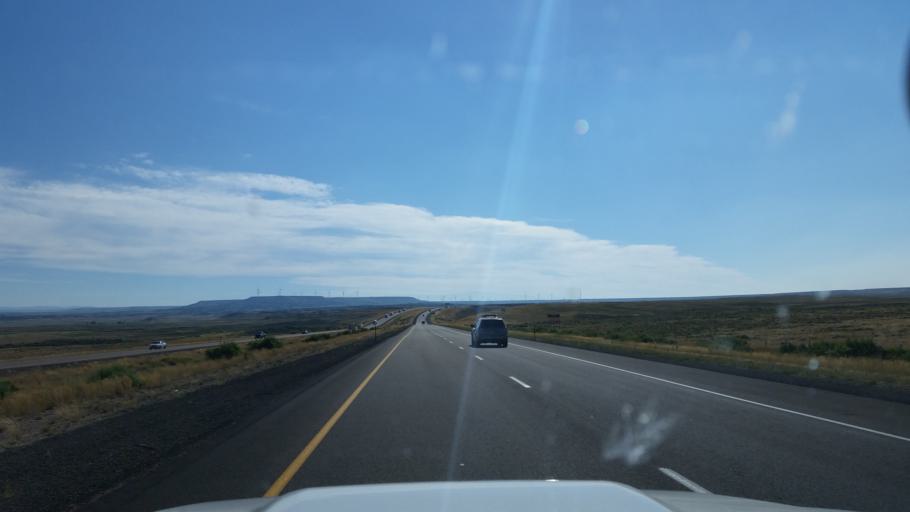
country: US
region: Wyoming
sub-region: Uinta County
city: Mountain View
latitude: 41.3433
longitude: -110.3959
